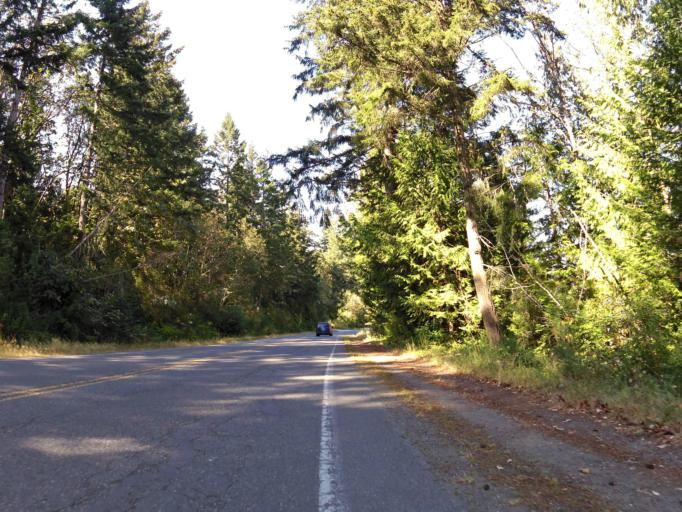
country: CA
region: British Columbia
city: North Saanich
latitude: 48.6296
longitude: -123.5301
